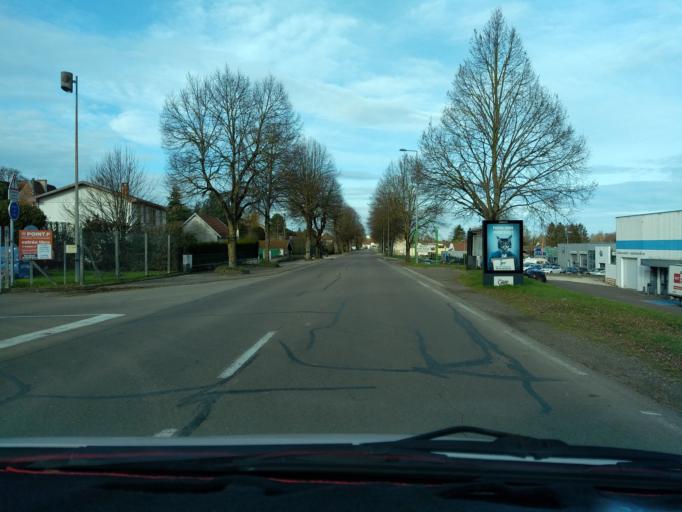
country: FR
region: Franche-Comte
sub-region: Departement de la Haute-Saone
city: Gray
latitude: 47.4367
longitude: 5.5993
